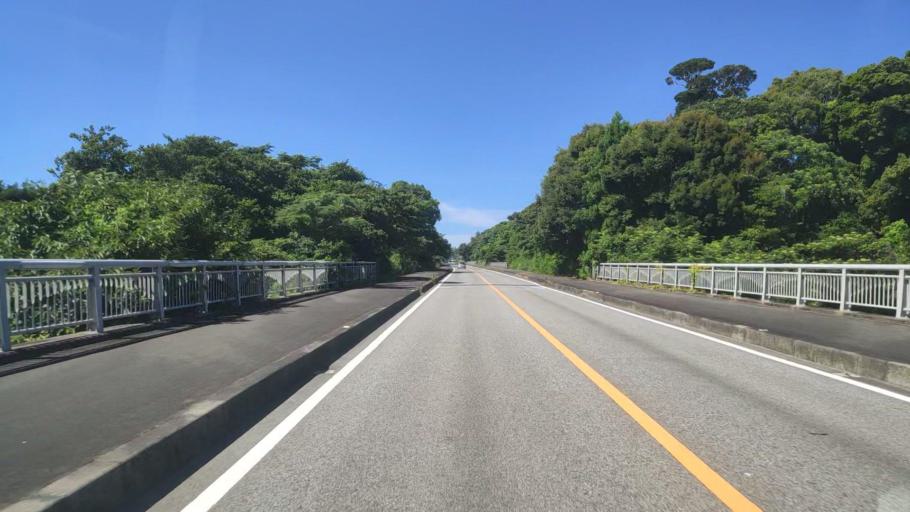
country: JP
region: Wakayama
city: Shingu
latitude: 33.7104
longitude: 135.9974
